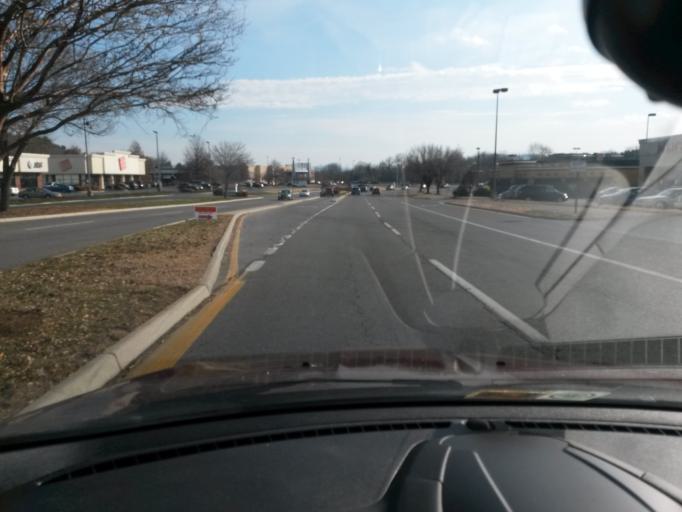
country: US
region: Virginia
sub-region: City of Roanoke
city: Roanoke
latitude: 37.3018
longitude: -79.9573
